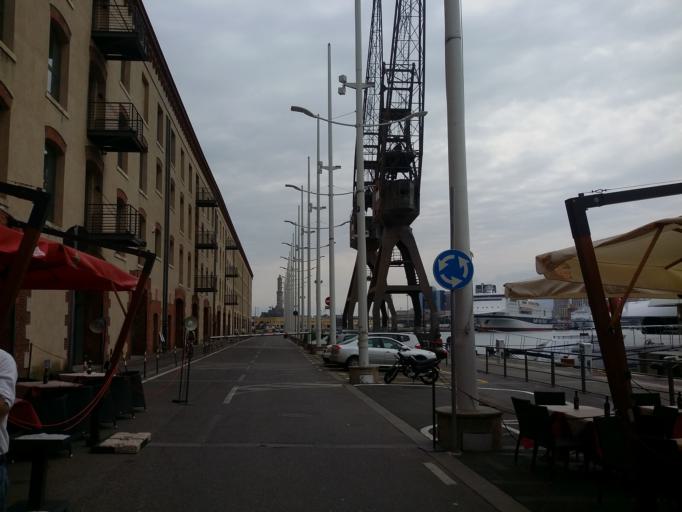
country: IT
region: Liguria
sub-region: Provincia di Genova
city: San Teodoro
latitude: 44.4085
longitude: 8.9214
